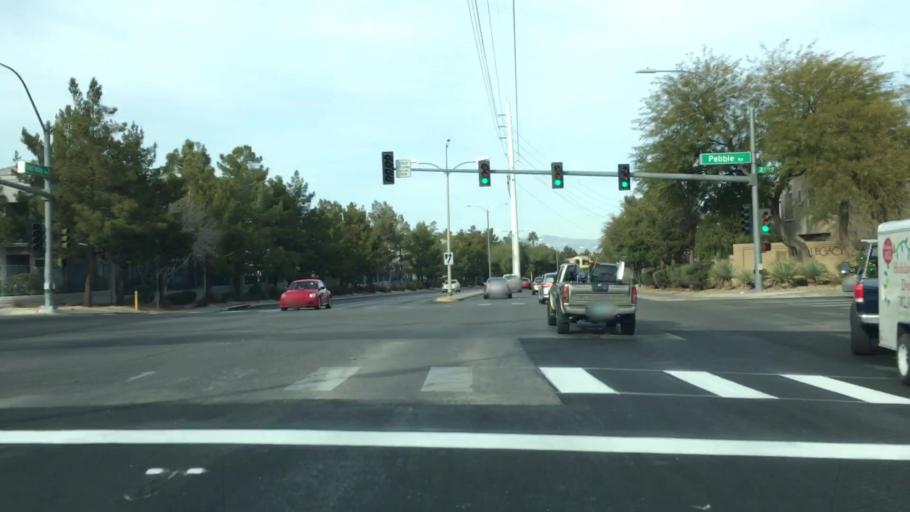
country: US
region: Nevada
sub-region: Clark County
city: Whitney
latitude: 36.0299
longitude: -115.0863
